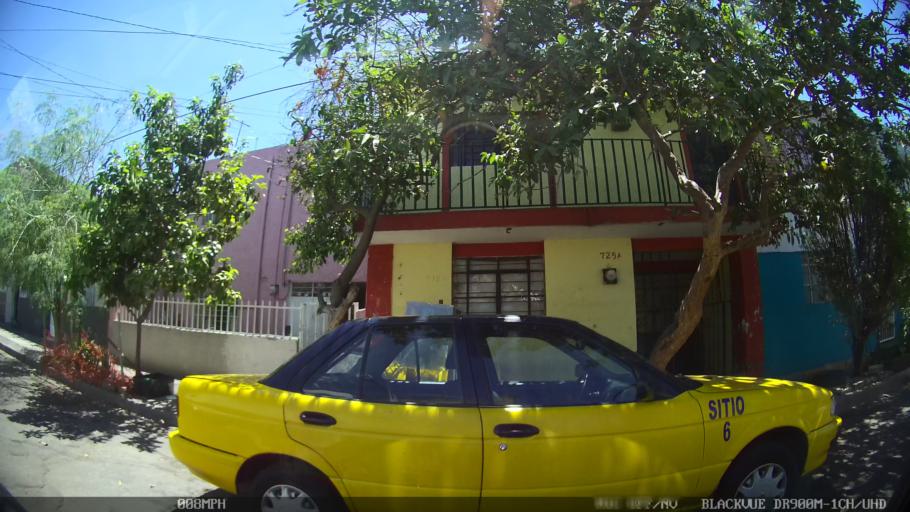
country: MX
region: Jalisco
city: Tlaquepaque
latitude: 20.6699
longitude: -103.2708
